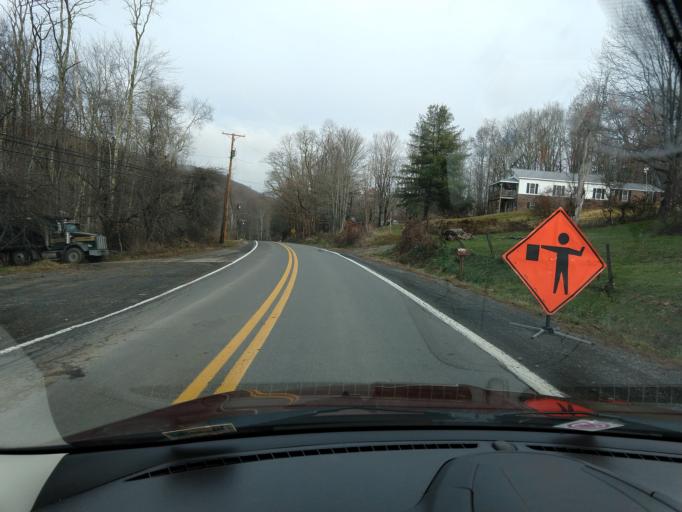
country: US
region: West Virginia
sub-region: Greenbrier County
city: Rainelle
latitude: 38.0622
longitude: -80.7079
